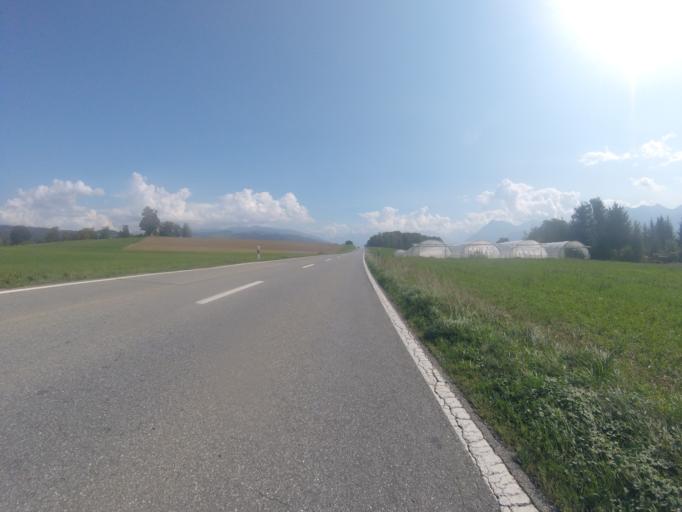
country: CH
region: Bern
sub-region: Thun District
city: Uttigen
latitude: 46.7894
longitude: 7.5683
